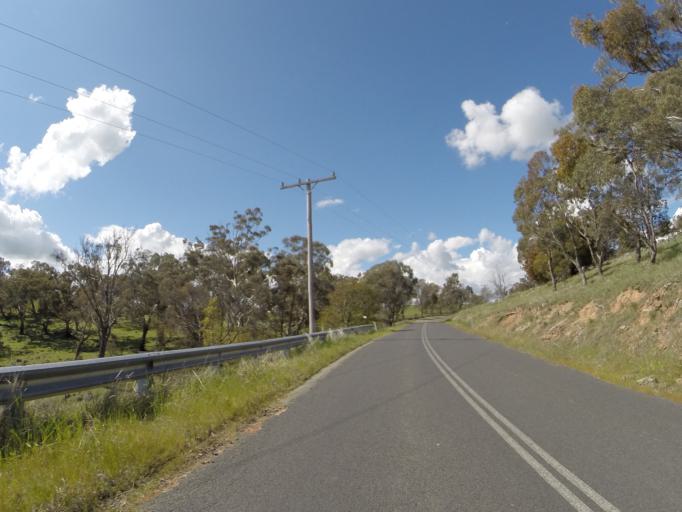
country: AU
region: New South Wales
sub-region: Yass Valley
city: Yass
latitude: -34.9831
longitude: 148.8434
